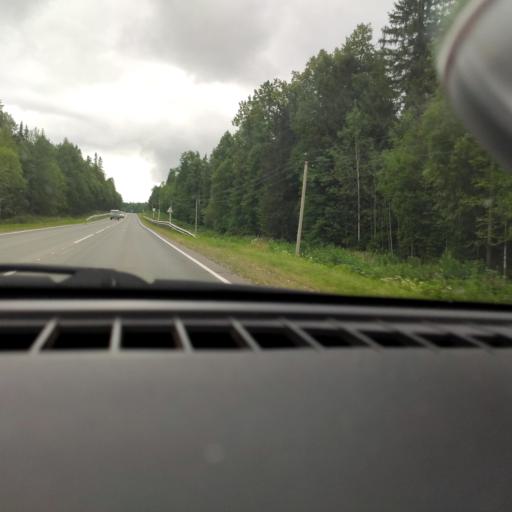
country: RU
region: Perm
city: Polazna
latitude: 58.3055
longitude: 56.1553
